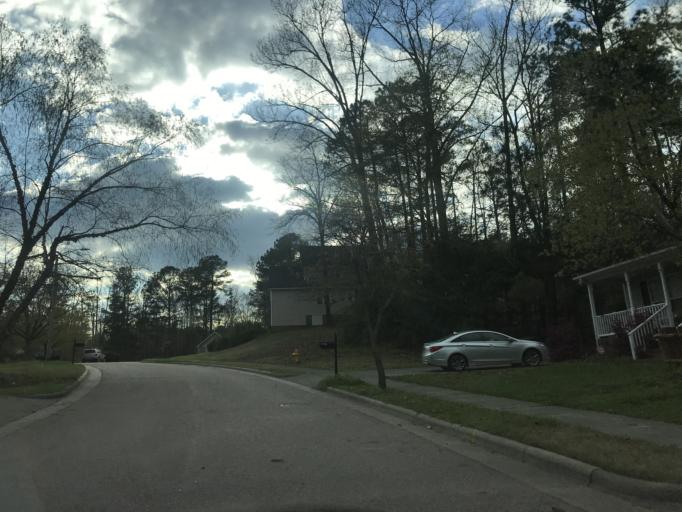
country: US
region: North Carolina
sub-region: Wake County
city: Knightdale
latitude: 35.8674
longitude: -78.5572
